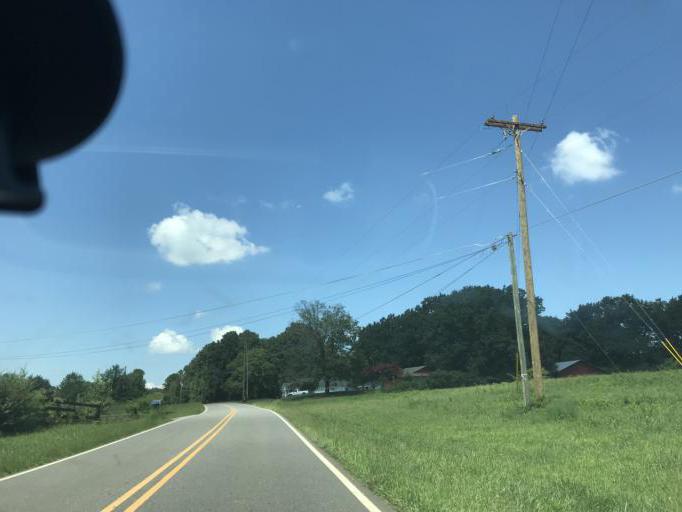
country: US
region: Georgia
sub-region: Dawson County
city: Dawsonville
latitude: 34.3186
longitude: -84.0095
